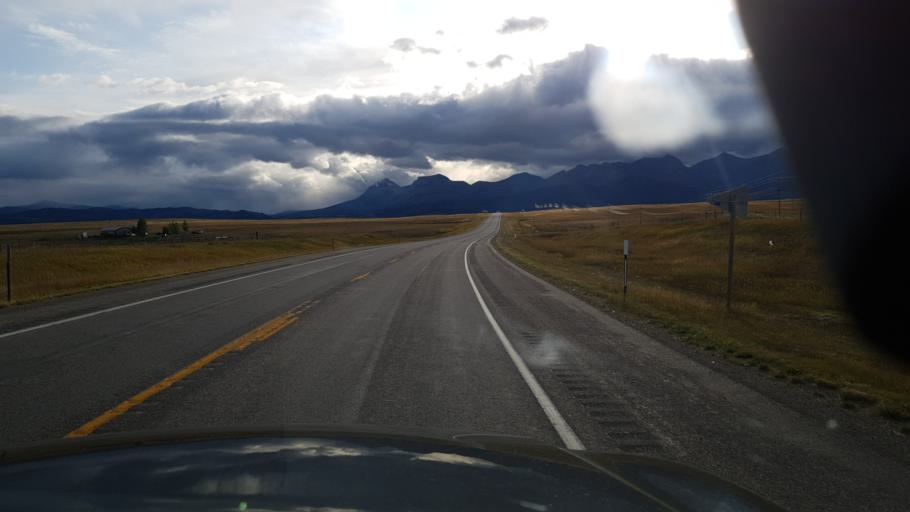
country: US
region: Montana
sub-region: Glacier County
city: South Browning
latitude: 48.4671
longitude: -113.1549
